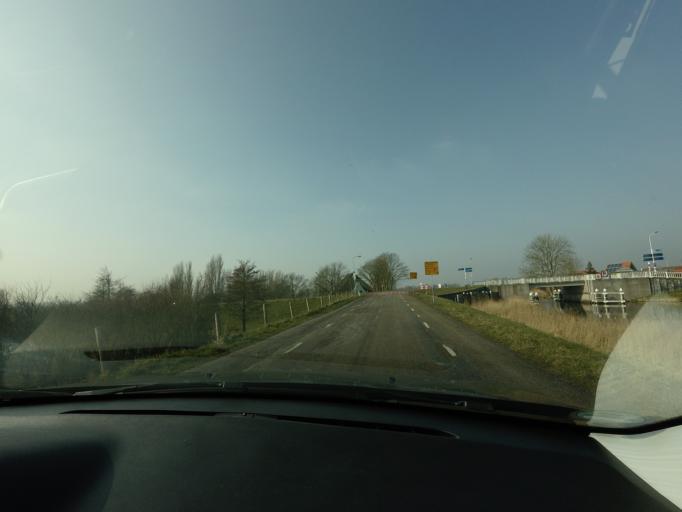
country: NL
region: North Holland
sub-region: Gemeente Heerhugowaard
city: Heerhugowaard
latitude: 52.6338
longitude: 4.8763
